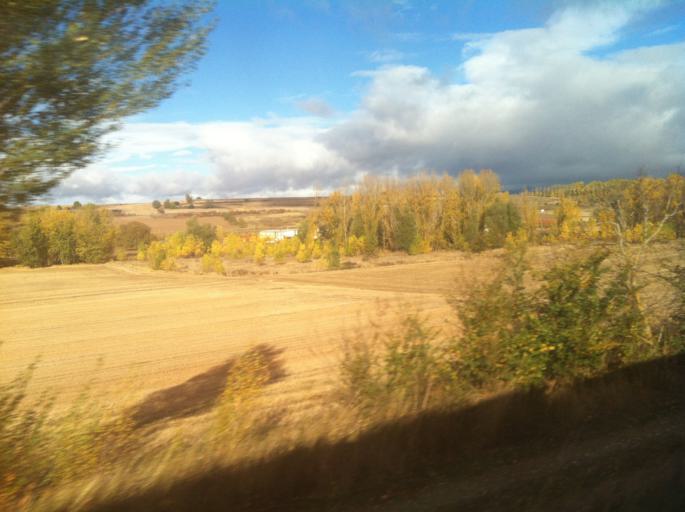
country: ES
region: Castille and Leon
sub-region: Provincia de Burgos
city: Briviesca
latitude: 42.5687
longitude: -3.3067
